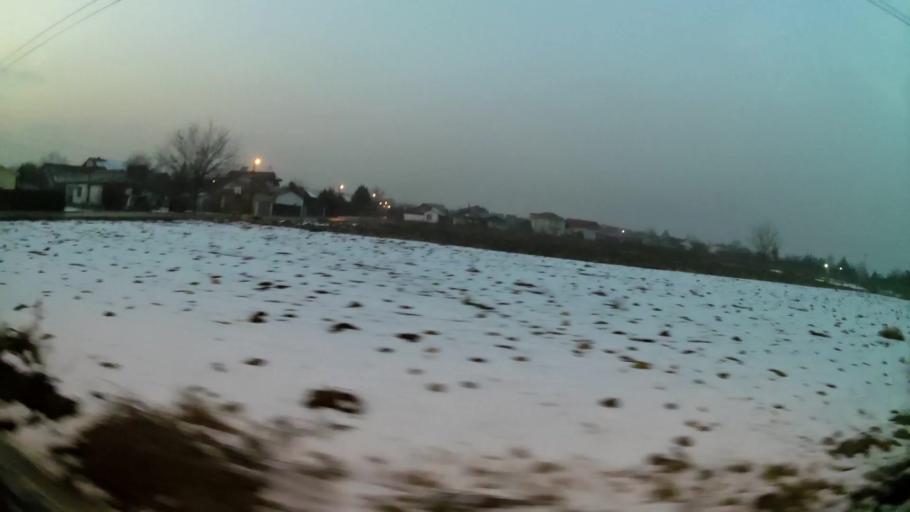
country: MK
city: Creshevo
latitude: 42.0055
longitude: 21.5133
